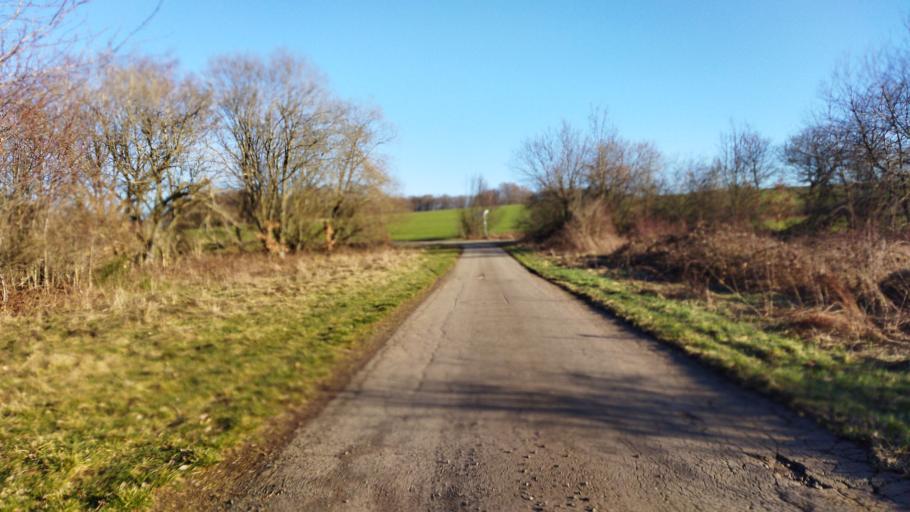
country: DE
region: Rheinland-Pfalz
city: Selchenbach
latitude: 49.4777
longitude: 7.3055
